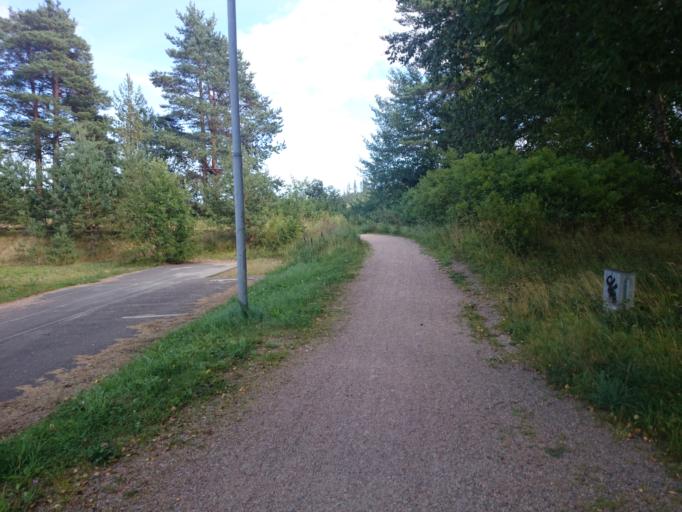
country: SE
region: Vaesternorrland
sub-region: Sundsvalls Kommun
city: Skottsund
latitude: 62.2953
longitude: 17.3821
